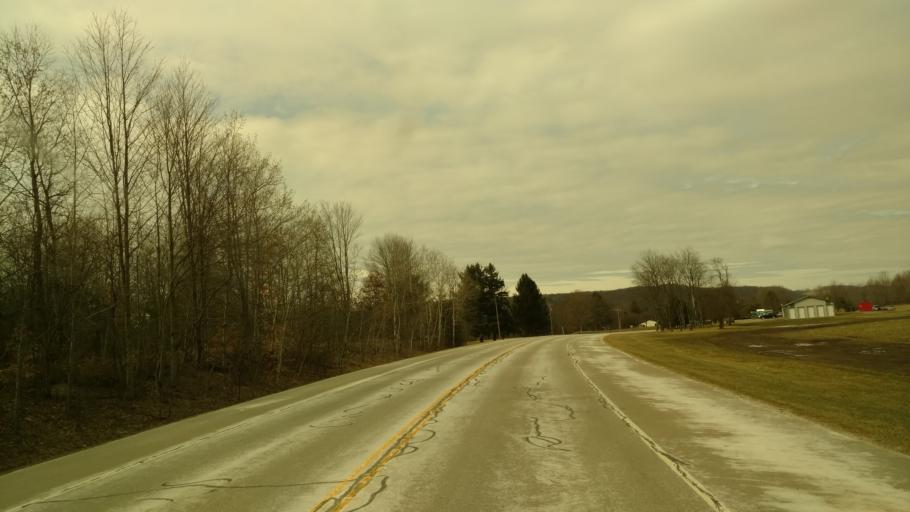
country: US
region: New York
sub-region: Allegany County
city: Wellsville
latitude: 42.0378
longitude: -77.9120
